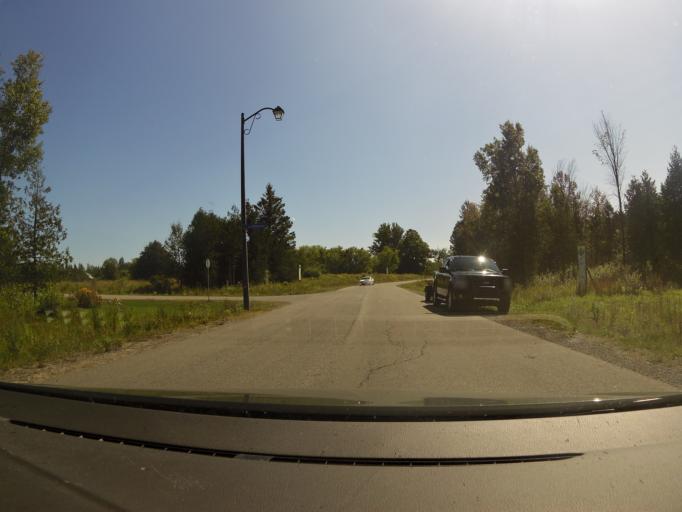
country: CA
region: Ontario
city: Bells Corners
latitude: 45.2768
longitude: -76.0071
